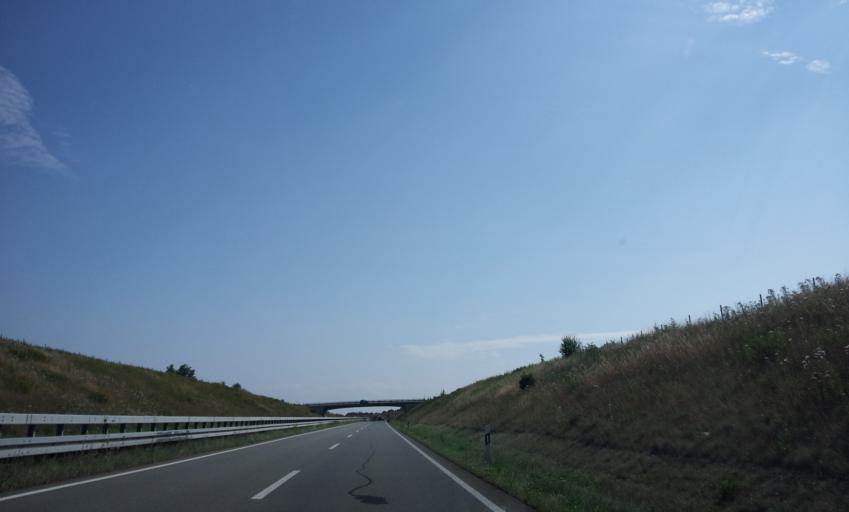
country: DE
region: Mecklenburg-Vorpommern
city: Brandshagen
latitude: 54.2205
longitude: 13.1529
